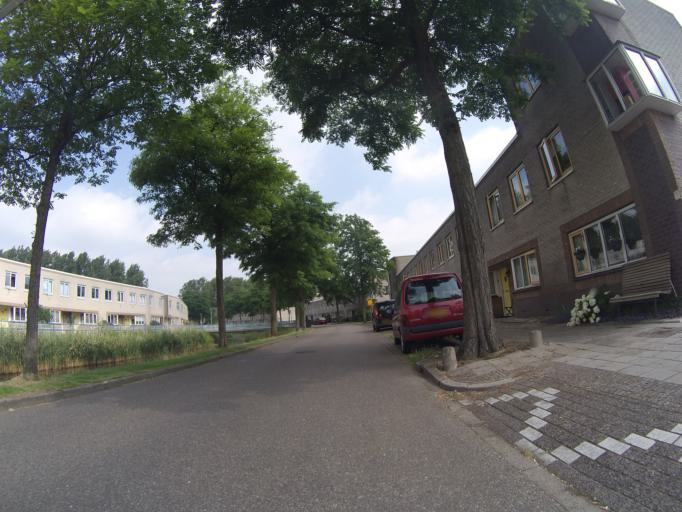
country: NL
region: Utrecht
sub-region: Gemeente Amersfoort
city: Randenbroek
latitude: 52.1839
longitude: 5.4100
